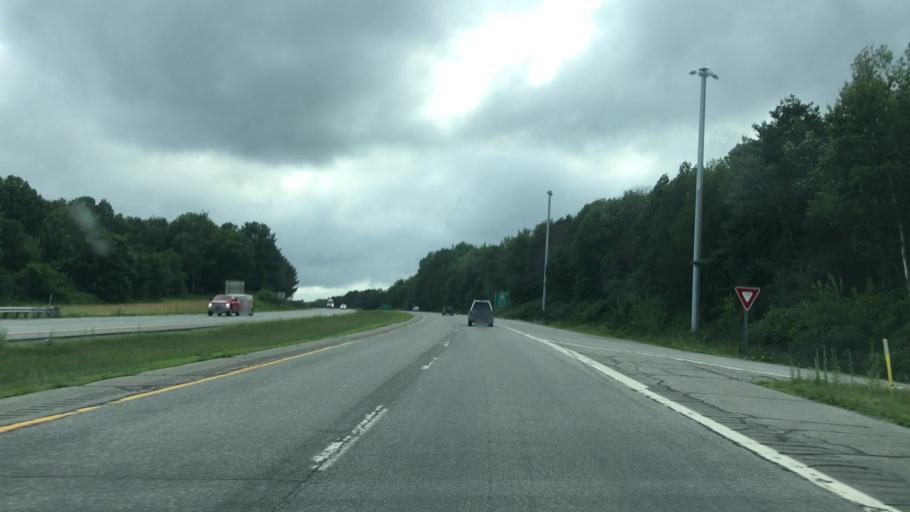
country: US
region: Maine
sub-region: Somerset County
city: Fairfield
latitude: 44.6015
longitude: -69.6023
